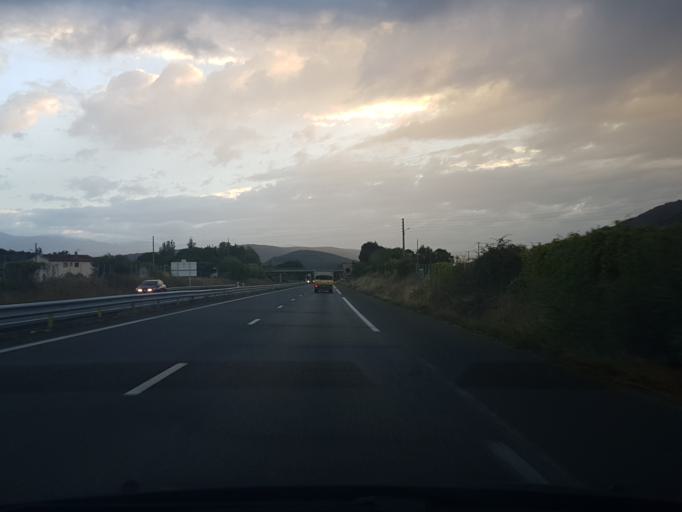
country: FR
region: Midi-Pyrenees
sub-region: Departement de l'Ariege
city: Varilhes
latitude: 43.0413
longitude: 1.6387
